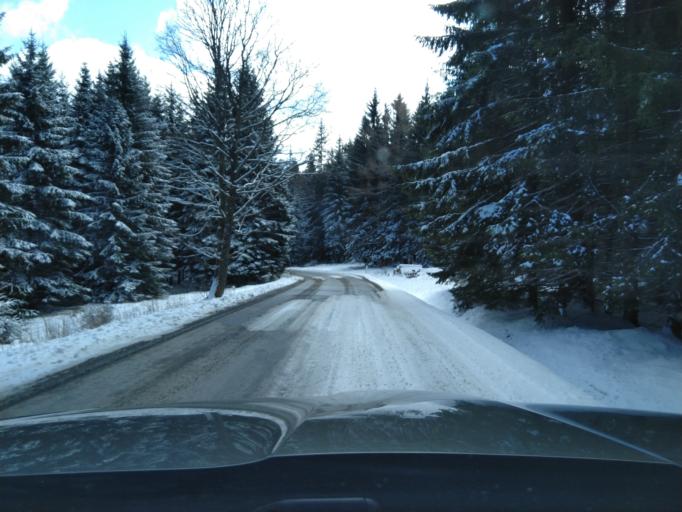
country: CZ
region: Jihocesky
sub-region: Okres Prachatice
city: Stachy
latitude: 49.0566
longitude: 13.6515
